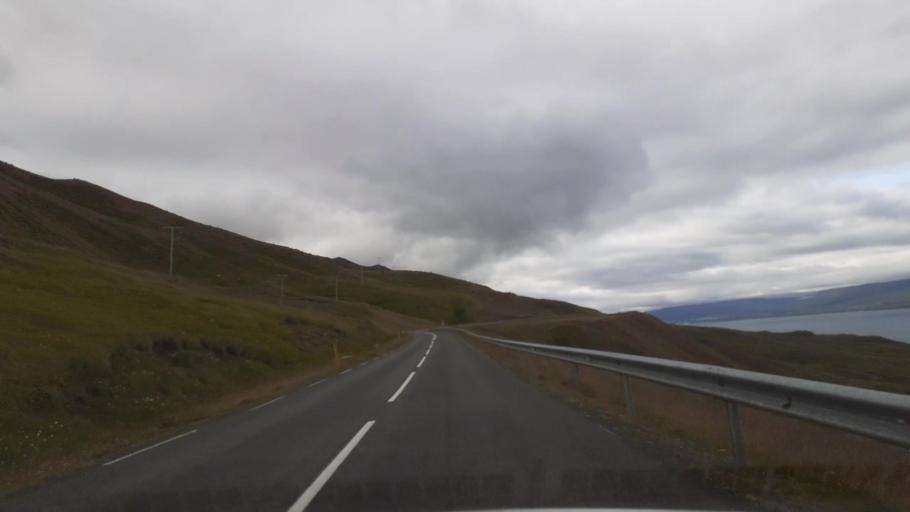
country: IS
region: Northeast
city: Akureyri
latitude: 65.8383
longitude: -18.0557
